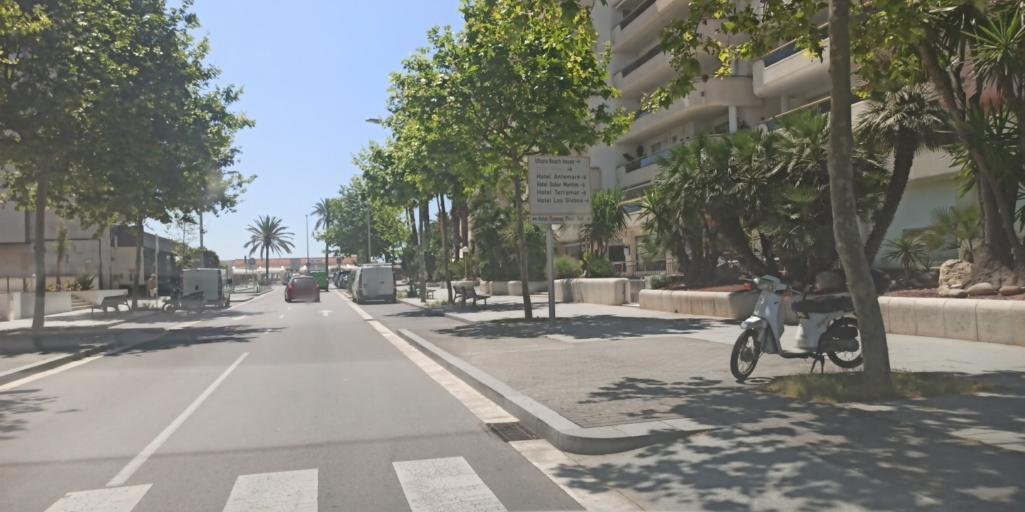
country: ES
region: Catalonia
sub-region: Provincia de Barcelona
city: Sitges
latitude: 41.2348
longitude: 1.8036
